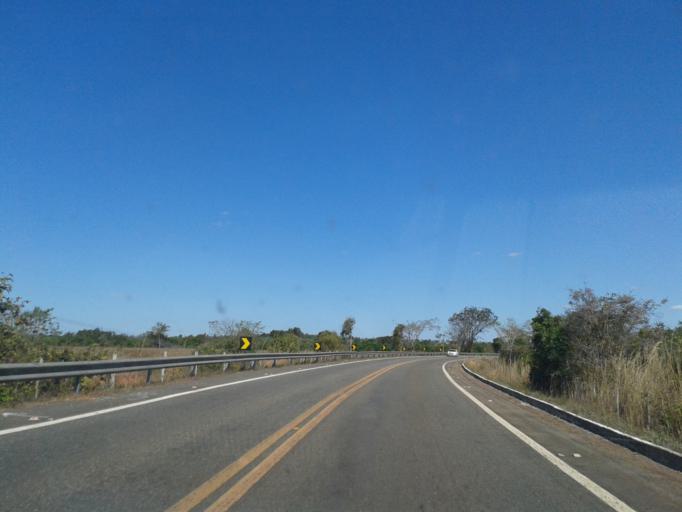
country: BR
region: Goias
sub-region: Sao Miguel Do Araguaia
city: Sao Miguel do Araguaia
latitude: -13.6293
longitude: -50.3120
